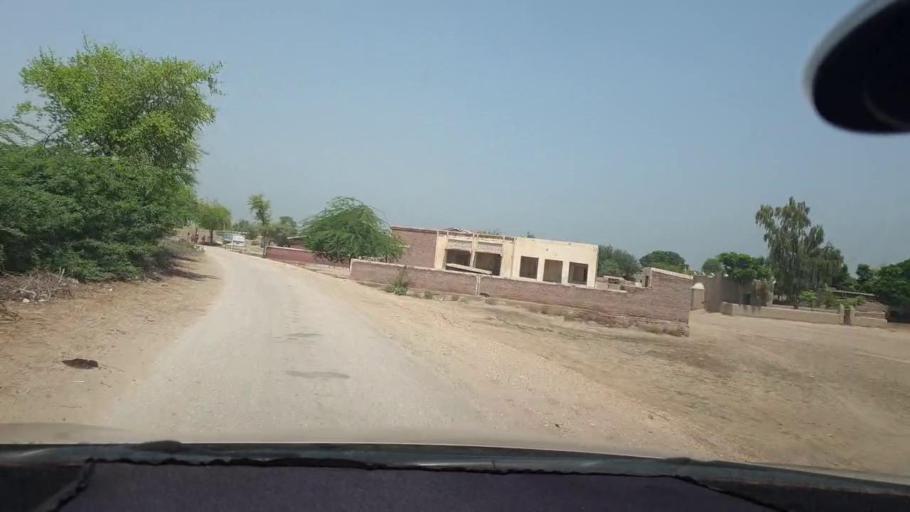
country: PK
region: Sindh
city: Kambar
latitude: 27.6651
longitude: 67.9152
